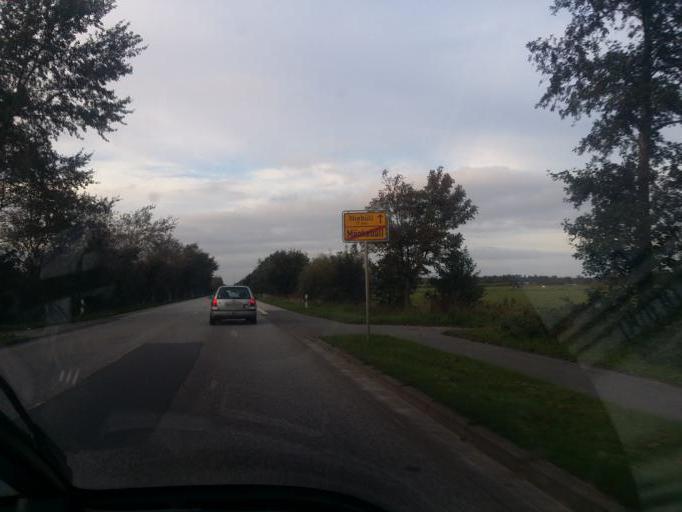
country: DE
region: Schleswig-Holstein
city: Bargum
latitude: 54.6885
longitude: 8.9574
